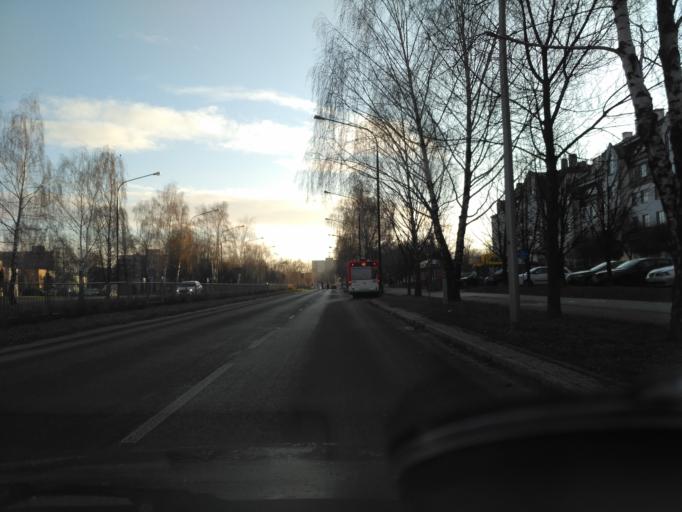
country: PL
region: Lublin Voivodeship
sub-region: Powiat lubelski
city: Lublin
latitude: 51.2673
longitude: 22.5435
